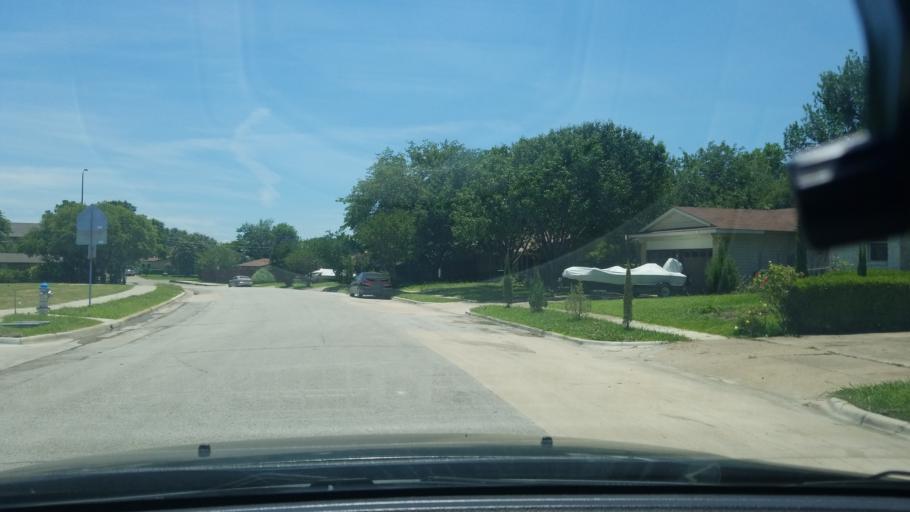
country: US
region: Texas
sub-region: Dallas County
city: Mesquite
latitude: 32.7747
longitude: -96.6113
